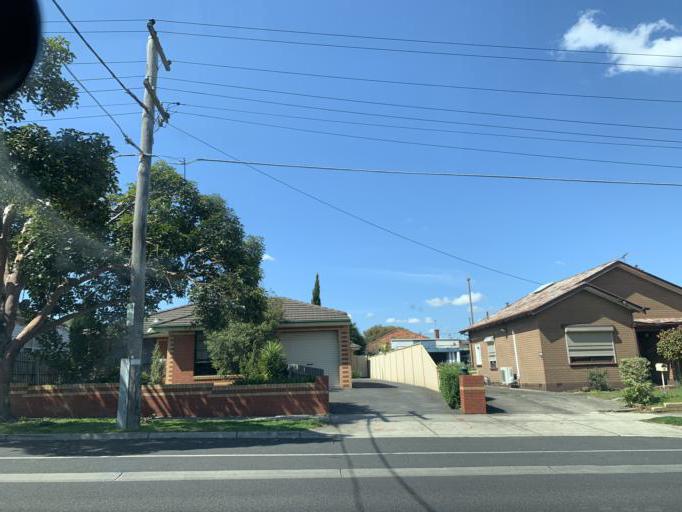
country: AU
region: Victoria
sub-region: Moreland
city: Pascoe Vale South
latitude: -37.7335
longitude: 144.9495
